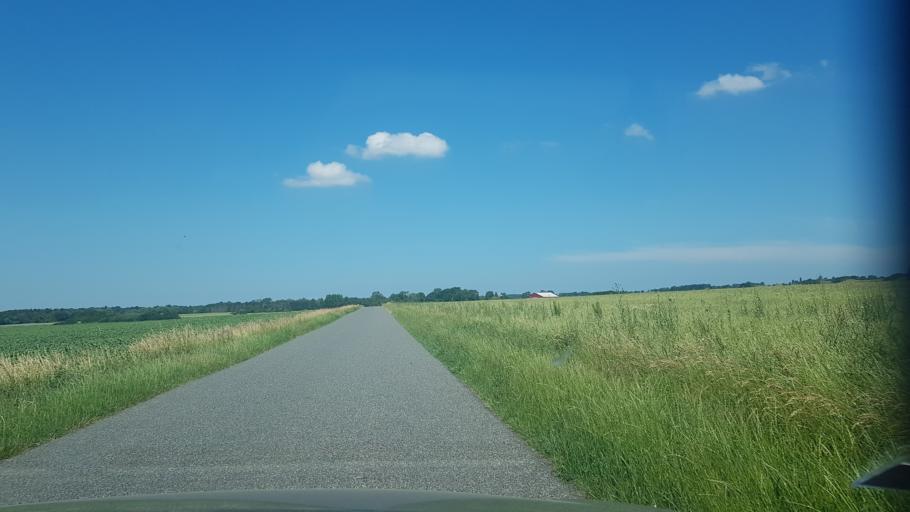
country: DK
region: Zealand
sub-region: Kalundborg Kommune
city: Svebolle
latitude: 55.6919
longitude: 11.3023
